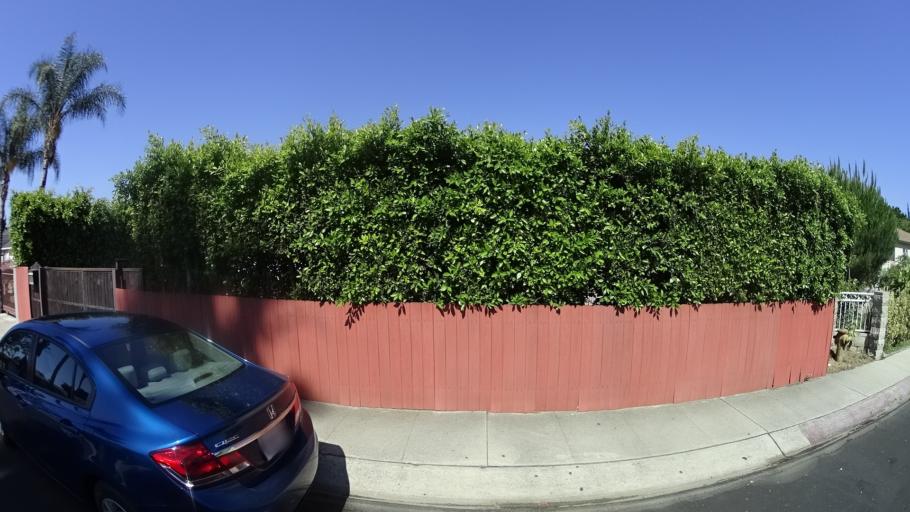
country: US
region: California
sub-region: Los Angeles County
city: Van Nuys
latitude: 34.2308
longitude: -118.4465
